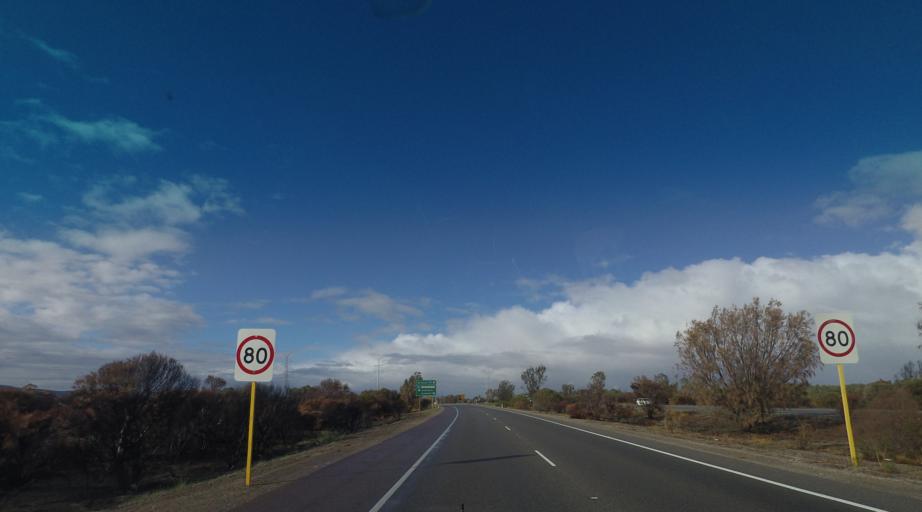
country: AU
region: Western Australia
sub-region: Armadale
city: Seville Grove
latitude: -32.1446
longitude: 115.9563
